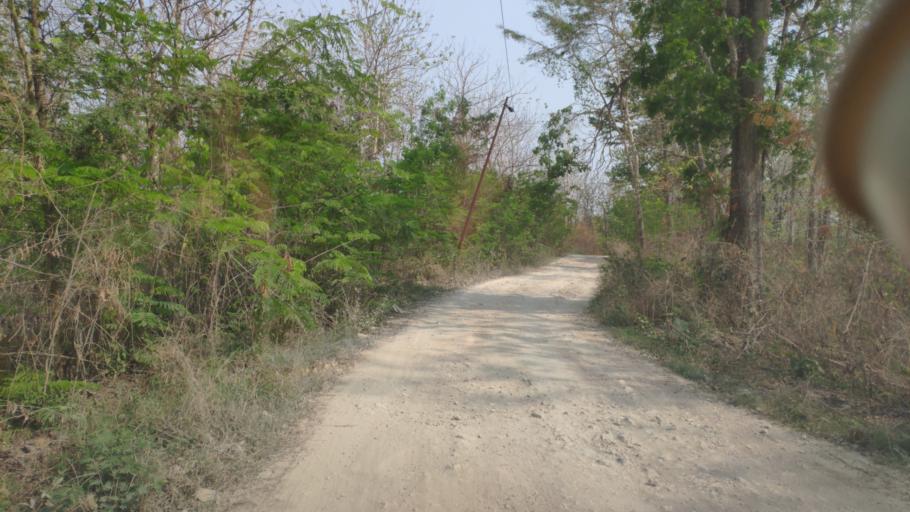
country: ID
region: Central Java
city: Randublatung
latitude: -7.2499
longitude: 111.2761
